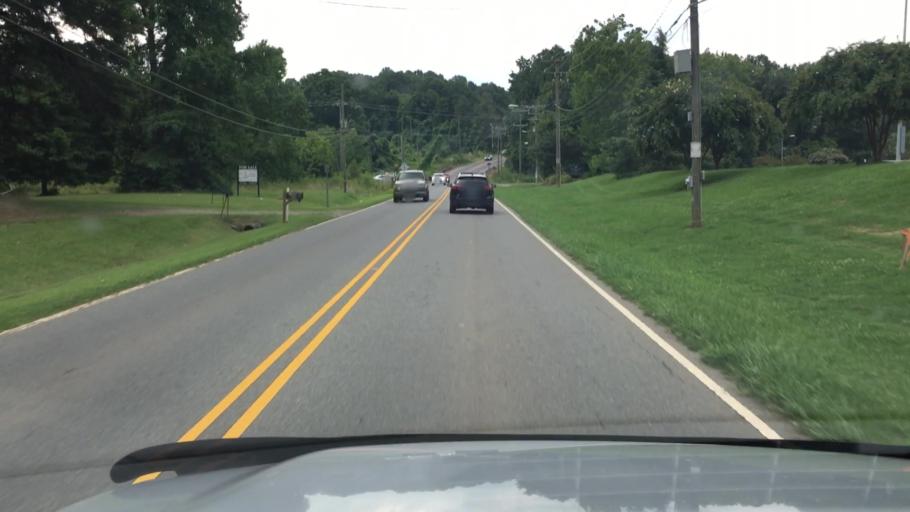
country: US
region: North Carolina
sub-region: Mecklenburg County
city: Huntersville
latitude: 35.3212
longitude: -80.8654
